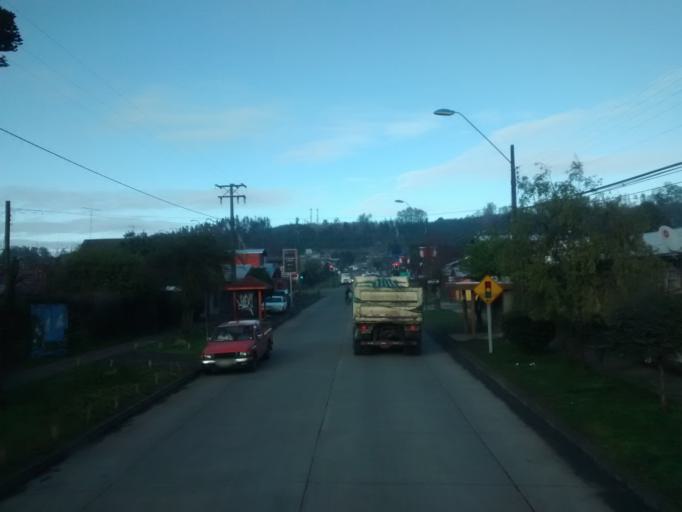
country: CL
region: Araucania
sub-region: Provincia de Cautin
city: Villarrica
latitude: -39.2784
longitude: -72.2325
